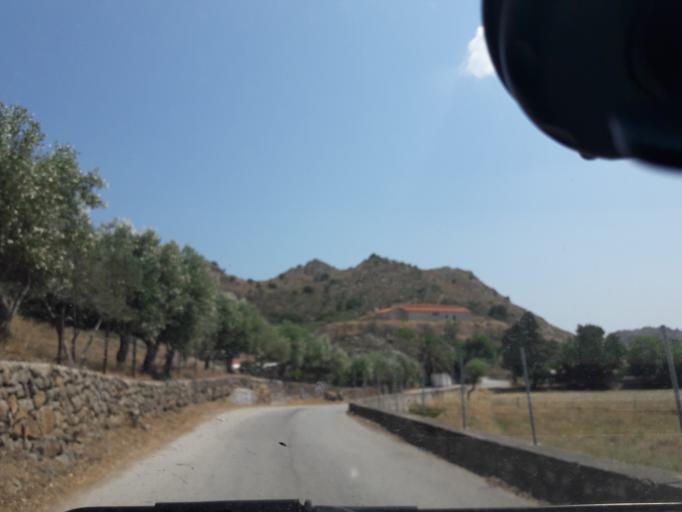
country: GR
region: North Aegean
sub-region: Nomos Lesvou
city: Myrina
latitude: 39.8479
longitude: 25.0849
